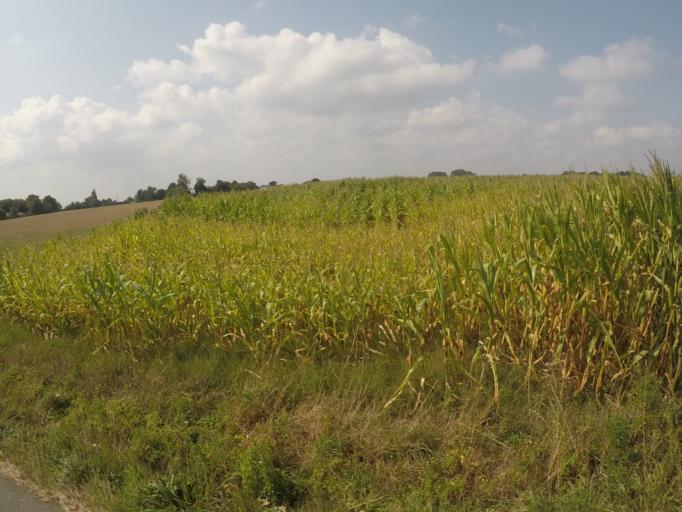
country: FR
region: Brittany
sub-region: Departement des Cotes-d'Armor
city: Tremuson
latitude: 48.5312
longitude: -2.8929
